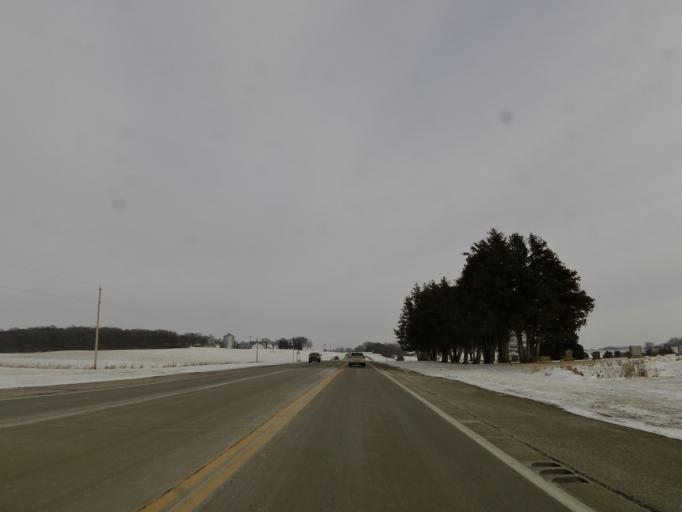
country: US
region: Minnesota
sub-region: McLeod County
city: Hutchinson
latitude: 44.8926
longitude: -94.2436
